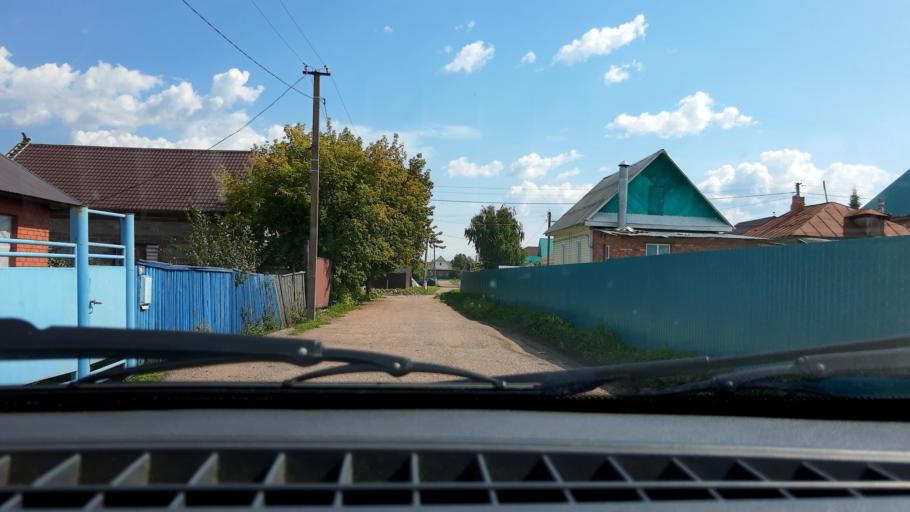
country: RU
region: Bashkortostan
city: Mikhaylovka
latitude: 54.8659
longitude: 55.8158
